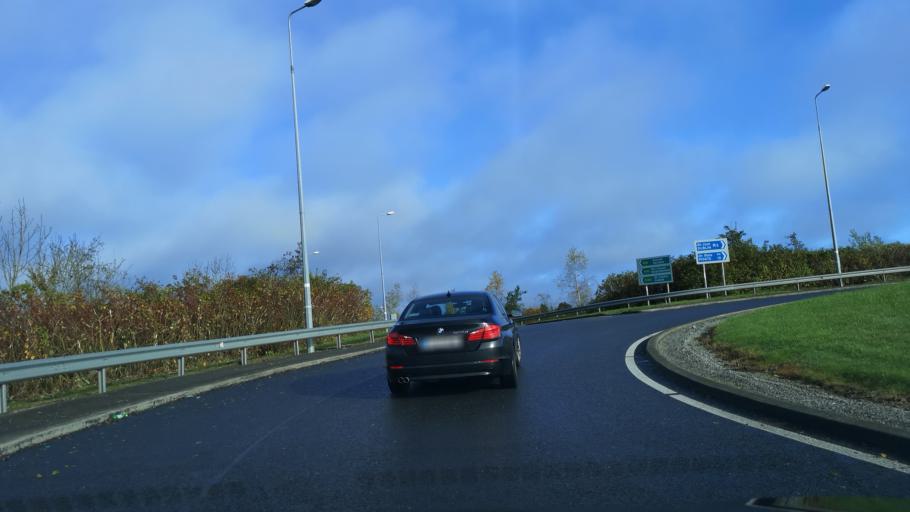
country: IE
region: Leinster
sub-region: An Iarmhi
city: Athlone
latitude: 53.4150
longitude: -7.8905
